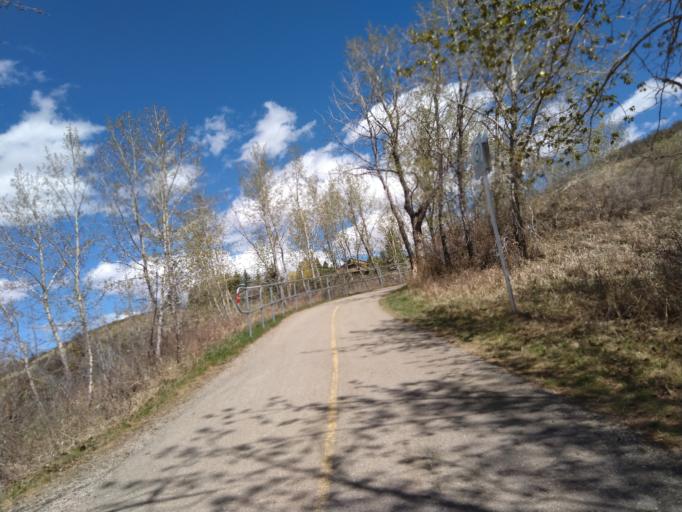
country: CA
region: Alberta
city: Calgary
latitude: 51.1020
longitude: -114.2014
